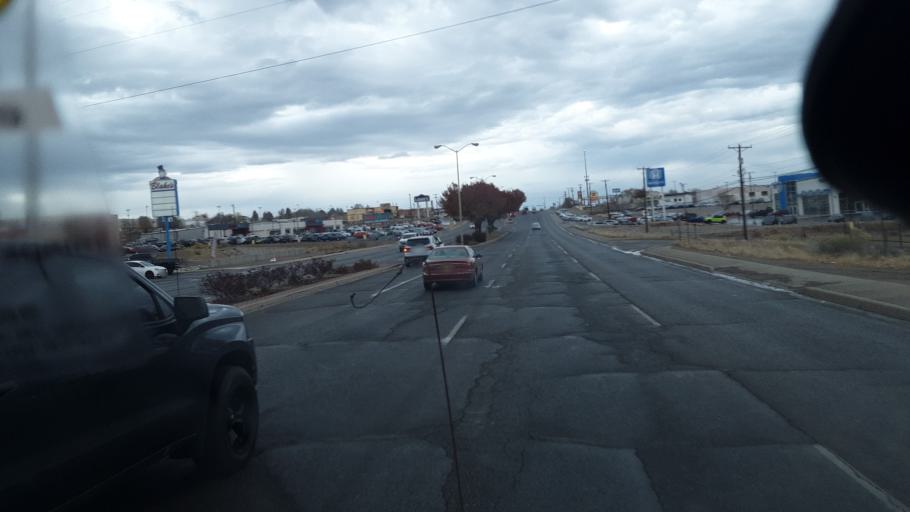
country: US
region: New Mexico
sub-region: San Juan County
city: Flora Vista
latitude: 36.7689
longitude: -108.1443
